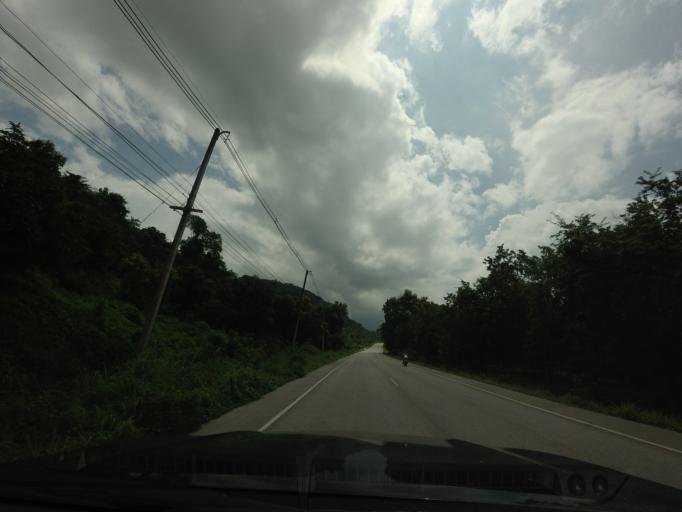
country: TH
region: Loei
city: Pak Chom
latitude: 18.0411
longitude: 101.7702
